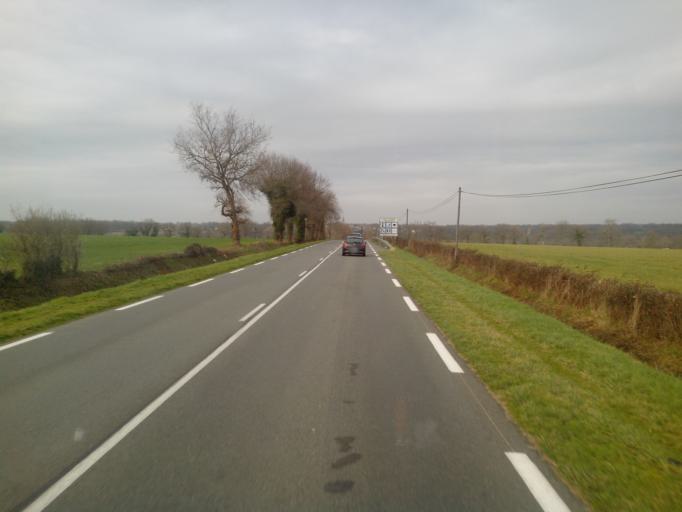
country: FR
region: Poitou-Charentes
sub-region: Departement de la Vienne
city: Saulge
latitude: 46.3188
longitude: 0.8228
